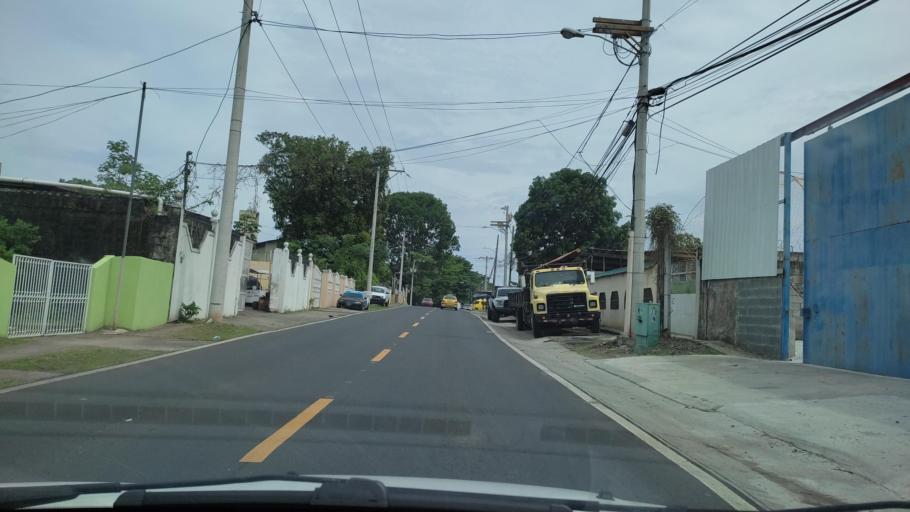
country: PA
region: Panama
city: San Miguelito
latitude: 9.0461
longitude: -79.4332
